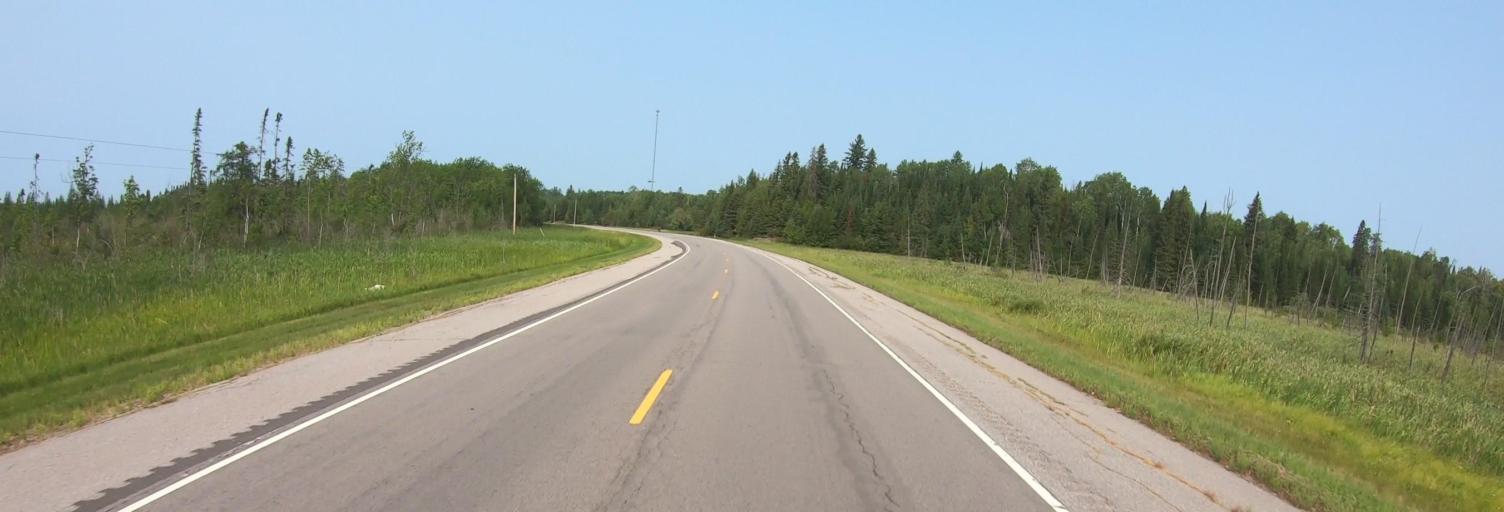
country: US
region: Minnesota
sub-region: Saint Louis County
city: Mountain Iron
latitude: 48.0903
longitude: -92.8254
